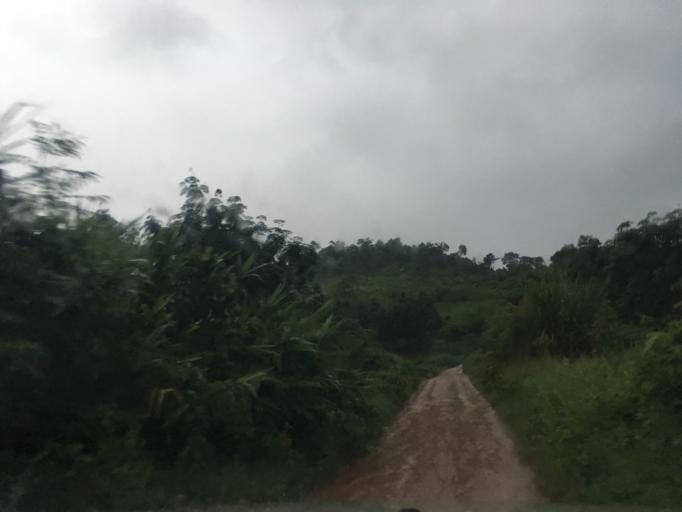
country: LA
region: Oudomxai
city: Muang La
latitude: 21.2516
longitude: 101.9318
